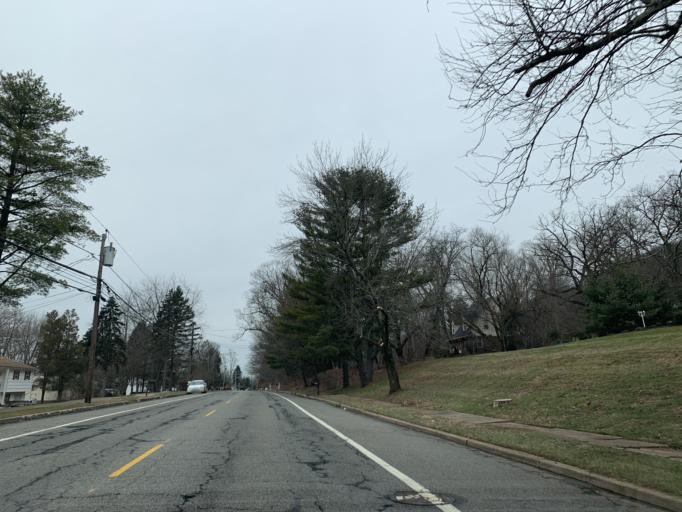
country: US
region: New Jersey
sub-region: Somerset County
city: Green Knoll
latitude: 40.6317
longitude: -74.6065
